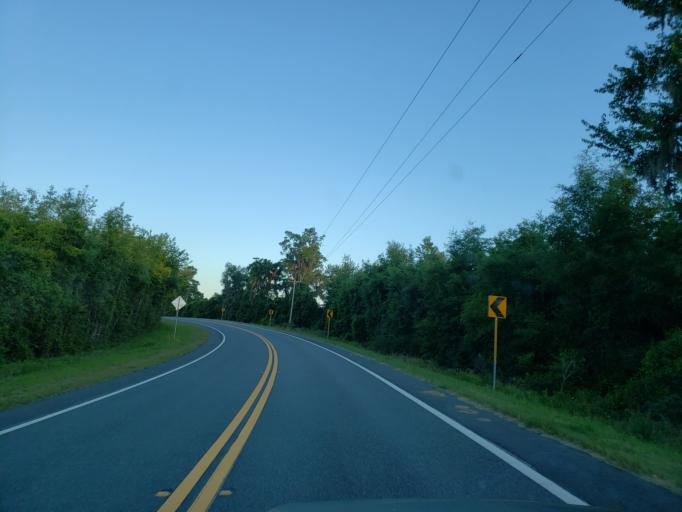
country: US
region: Florida
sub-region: Madison County
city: Madison
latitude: 30.5822
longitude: -83.2405
